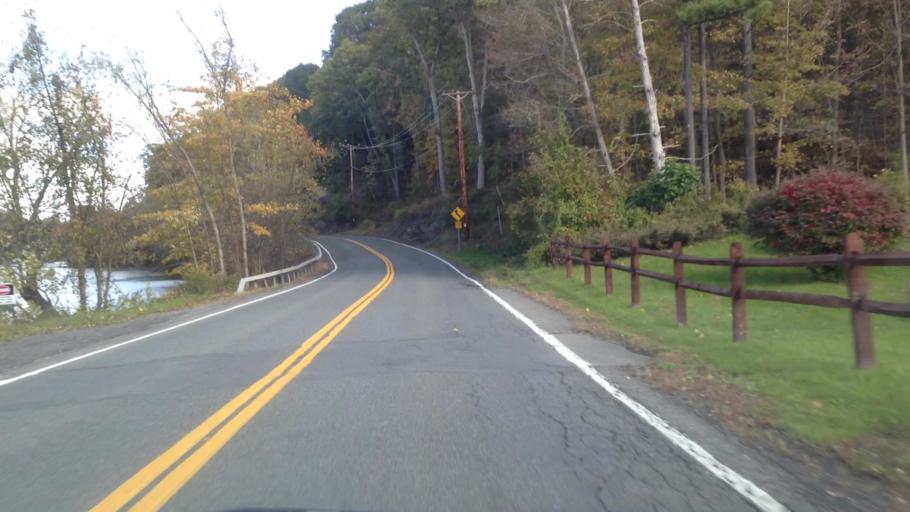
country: US
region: New York
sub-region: Ulster County
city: Tillson
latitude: 41.8179
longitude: -74.0546
